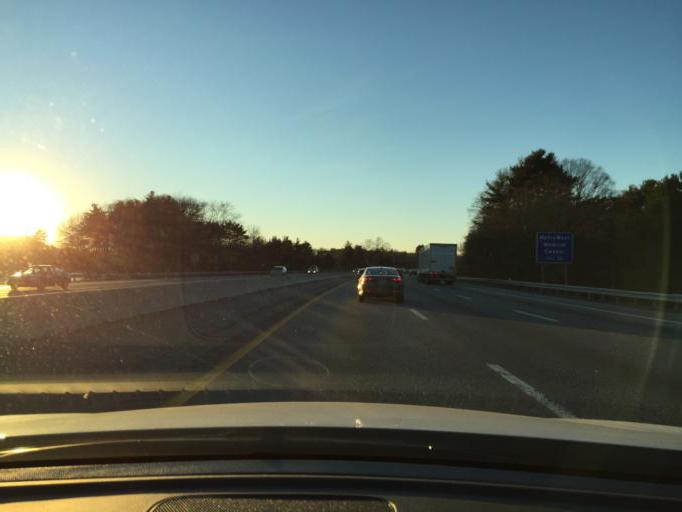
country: US
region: Massachusetts
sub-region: Middlesex County
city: Cochituate
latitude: 42.3113
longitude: -71.3695
